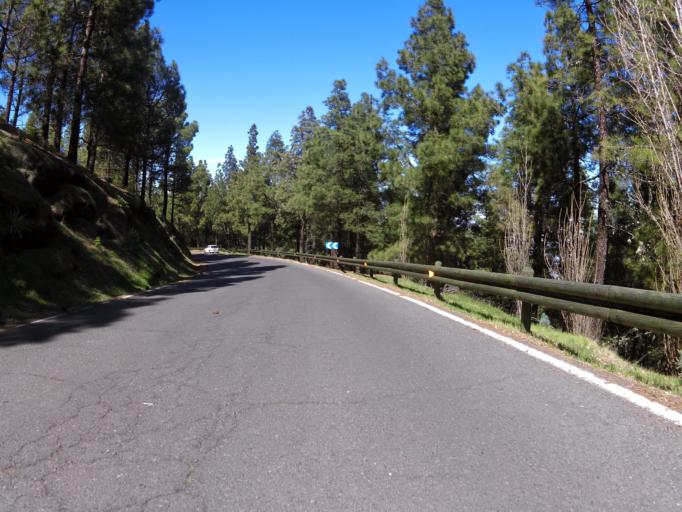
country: ES
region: Canary Islands
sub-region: Provincia de Las Palmas
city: Tejeda
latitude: 27.9846
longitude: -15.5787
